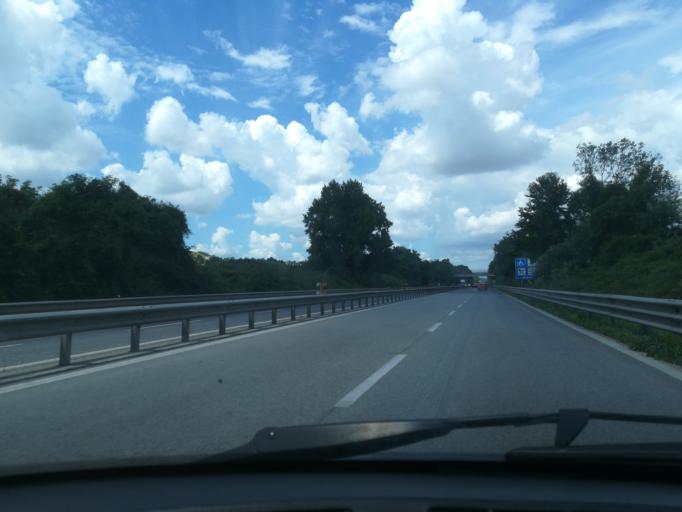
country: IT
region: The Marches
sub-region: Provincia di Macerata
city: Villa San Filippo
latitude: 43.2635
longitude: 13.5792
